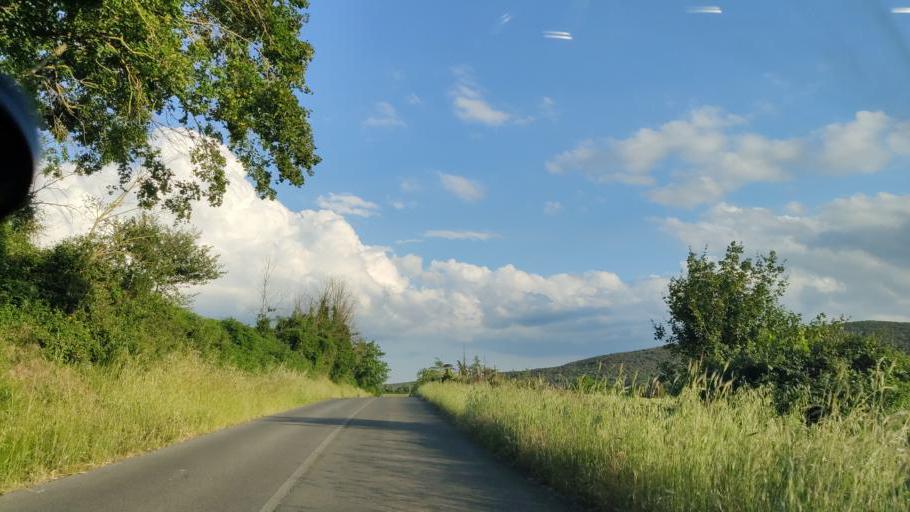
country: IT
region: Umbria
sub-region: Provincia di Terni
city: Amelia
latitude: 42.5845
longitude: 12.3830
